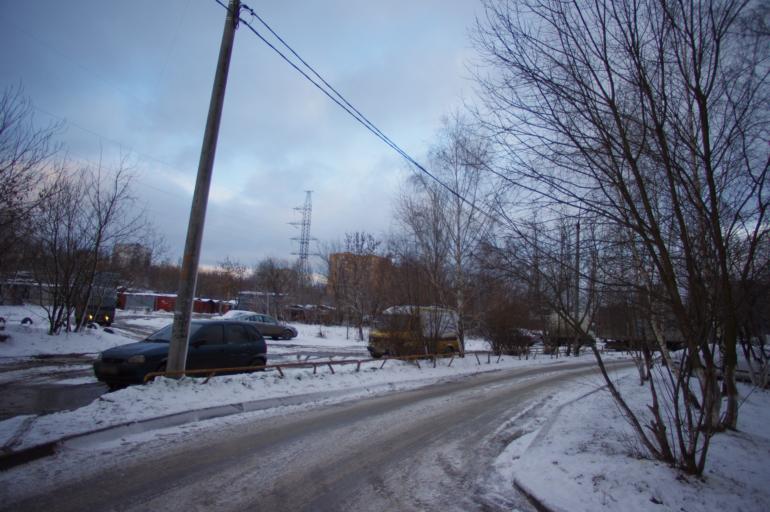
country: RU
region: Moskovskaya
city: Krasnogorsk
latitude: 55.8100
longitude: 37.3222
